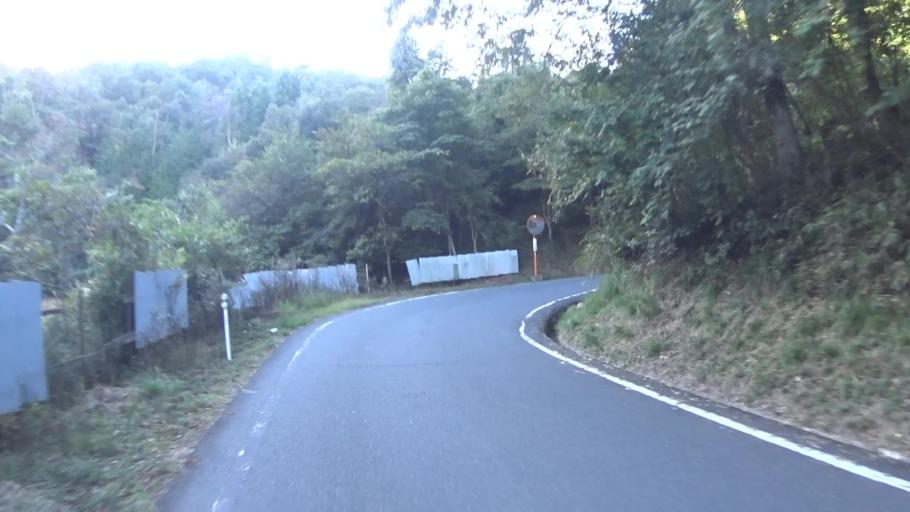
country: JP
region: Hyogo
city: Toyooka
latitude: 35.6150
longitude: 134.8730
